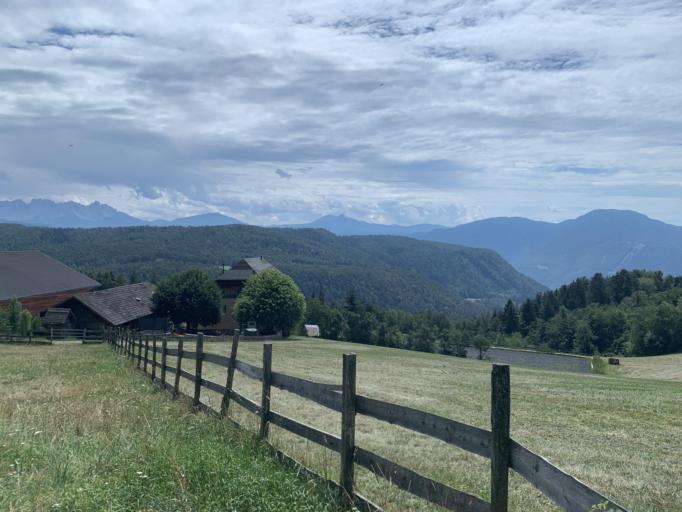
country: IT
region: Trentino-Alto Adige
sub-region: Bolzano
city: Soprabolzano
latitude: 46.5300
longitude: 11.4115
